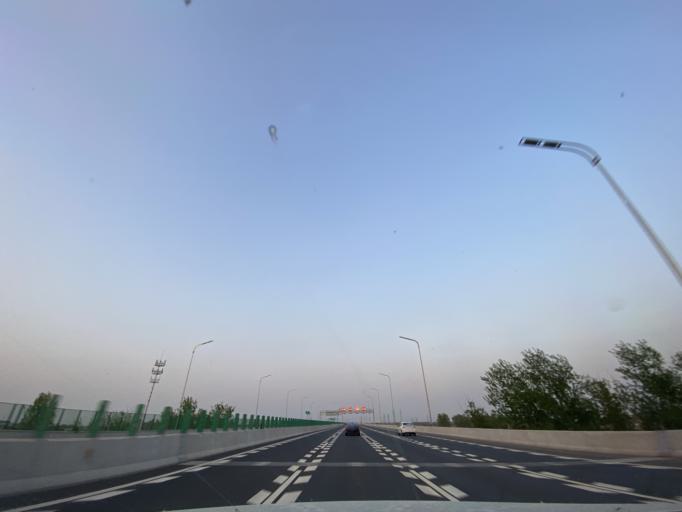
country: CN
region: Beijing
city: Xingfeng
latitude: 39.6921
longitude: 116.3700
